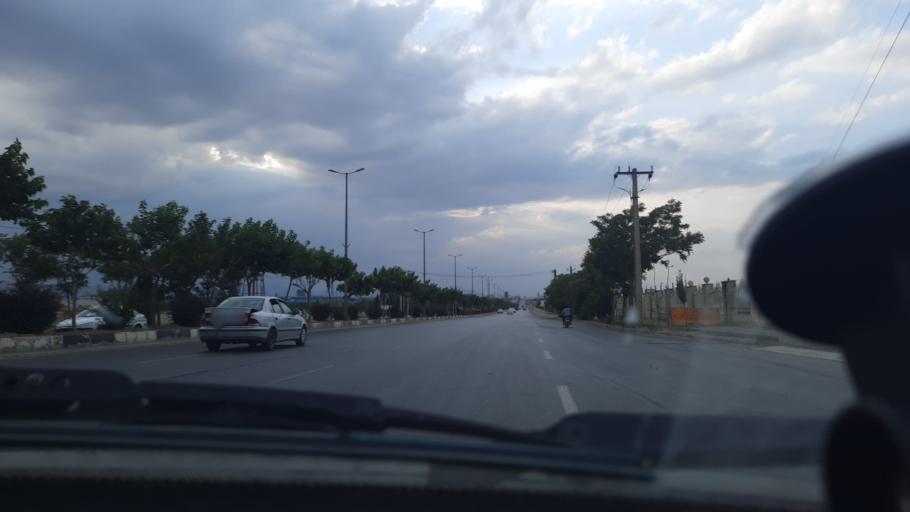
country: IR
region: Markazi
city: Arak
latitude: 34.0738
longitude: 49.7754
